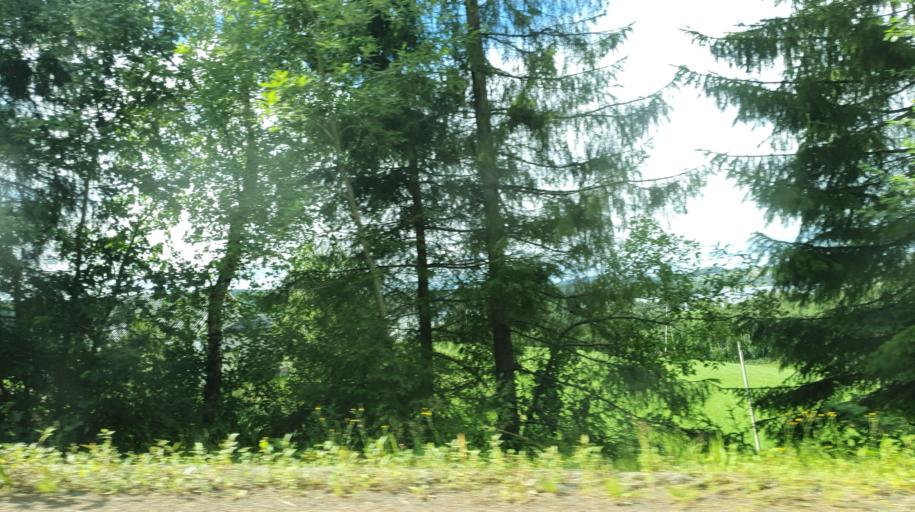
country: NO
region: Nord-Trondelag
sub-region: Levanger
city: Skogn
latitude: 63.6124
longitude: 11.2796
